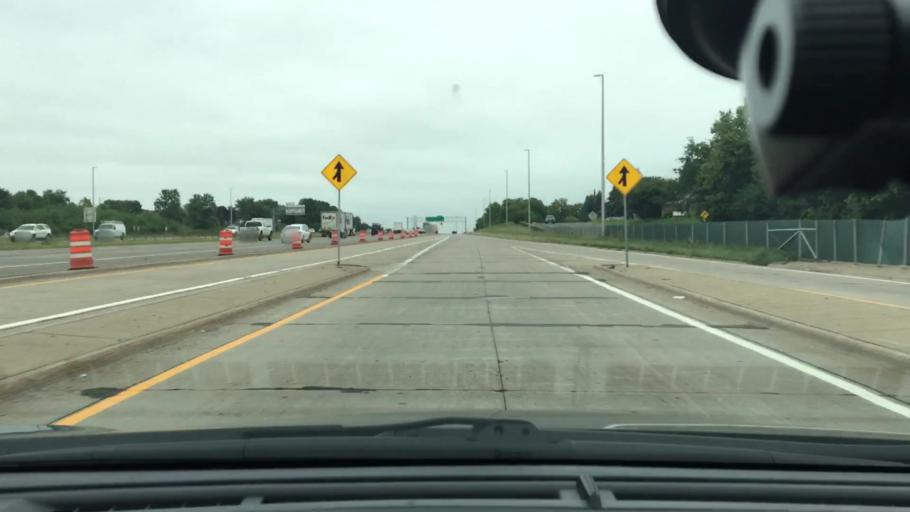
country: US
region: Minnesota
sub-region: Hennepin County
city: Maple Grove
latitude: 45.1035
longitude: -93.4593
